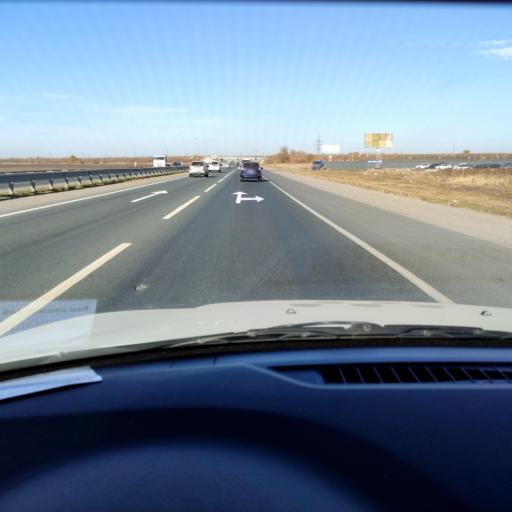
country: RU
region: Samara
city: Tol'yatti
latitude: 53.5584
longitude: 49.5010
